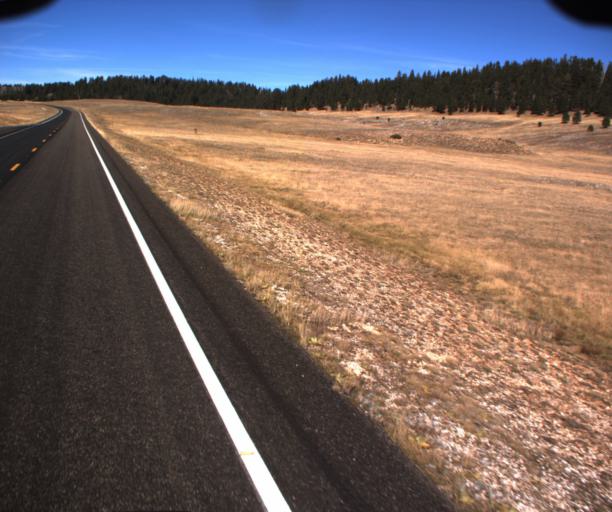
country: US
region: Arizona
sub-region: Coconino County
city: Grand Canyon
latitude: 36.4925
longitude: -112.1312
